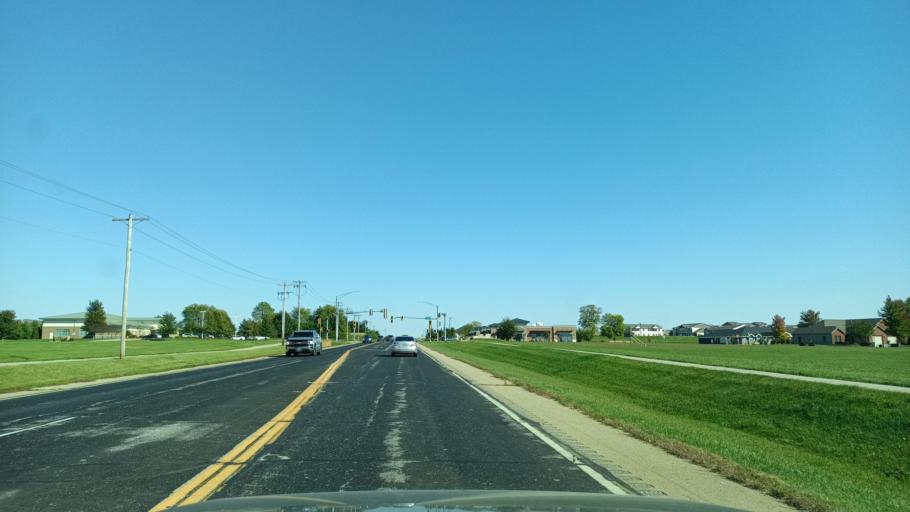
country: US
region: Illinois
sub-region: Champaign County
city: Lake of the Woods
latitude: 40.1865
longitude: -88.3791
